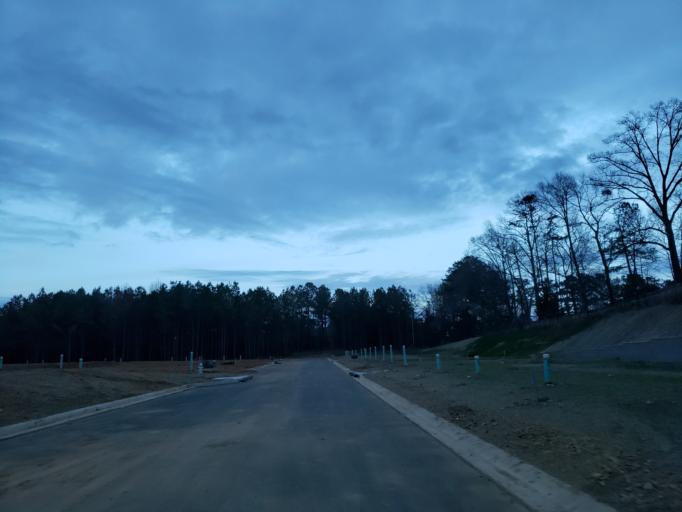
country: US
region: Georgia
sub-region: Cobb County
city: Kennesaw
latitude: 34.0273
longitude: -84.6286
